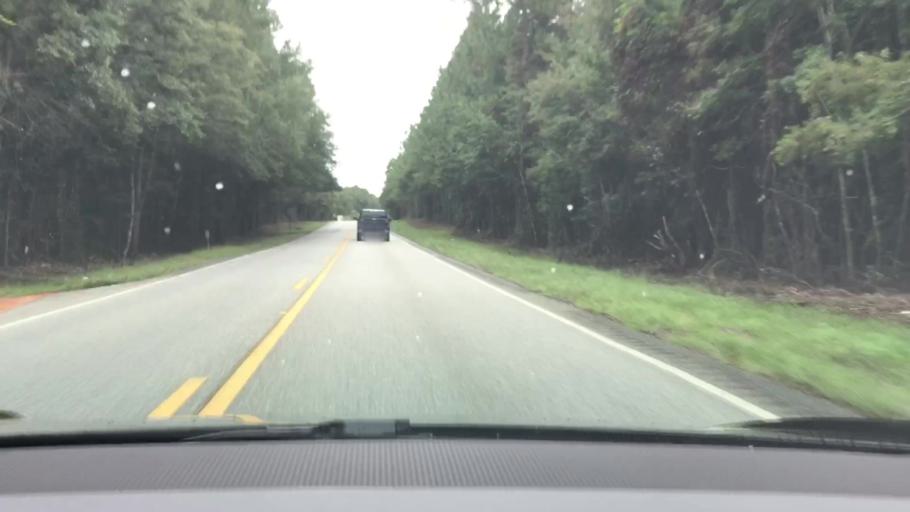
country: US
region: Alabama
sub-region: Geneva County
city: Samson
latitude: 30.9959
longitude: -86.1326
